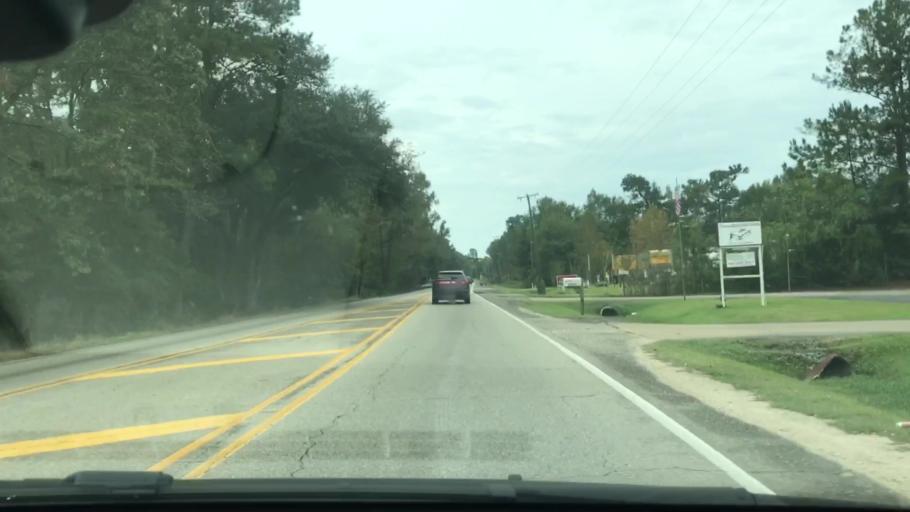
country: US
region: Louisiana
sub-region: Saint Tammany Parish
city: Slidell
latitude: 30.3012
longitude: -89.7742
